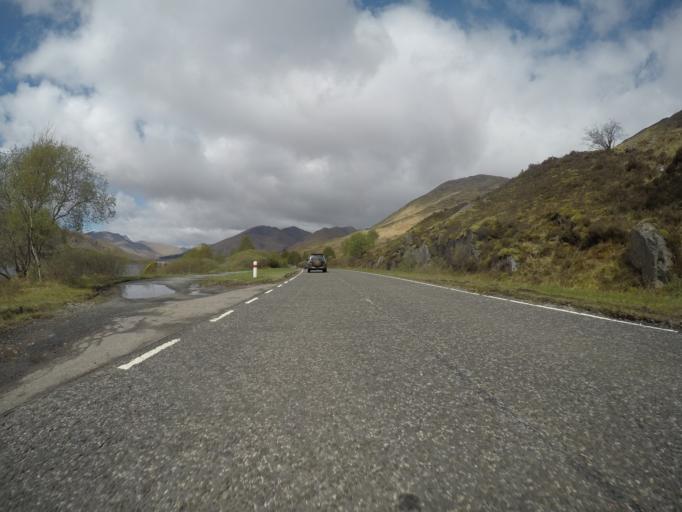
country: GB
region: Scotland
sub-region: Highland
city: Spean Bridge
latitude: 57.1528
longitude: -5.1274
